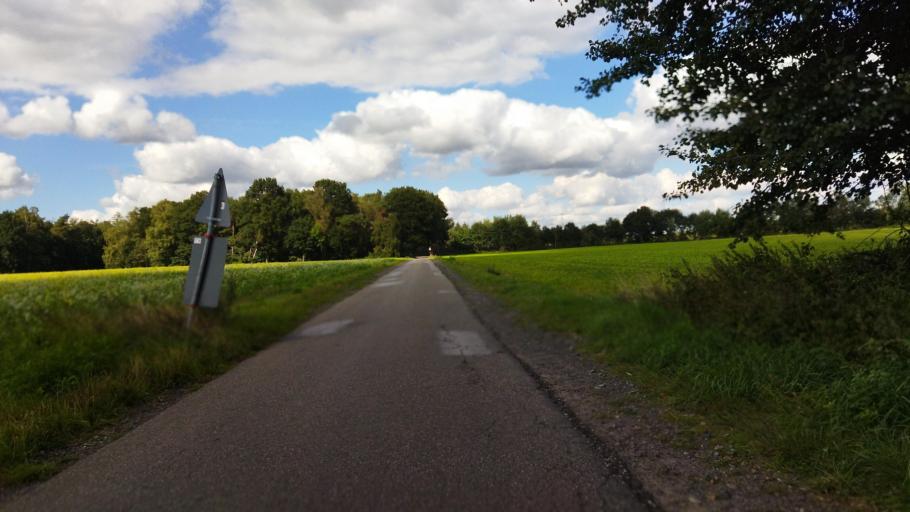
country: DE
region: Lower Saxony
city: Lingen
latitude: 52.4662
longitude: 7.3403
